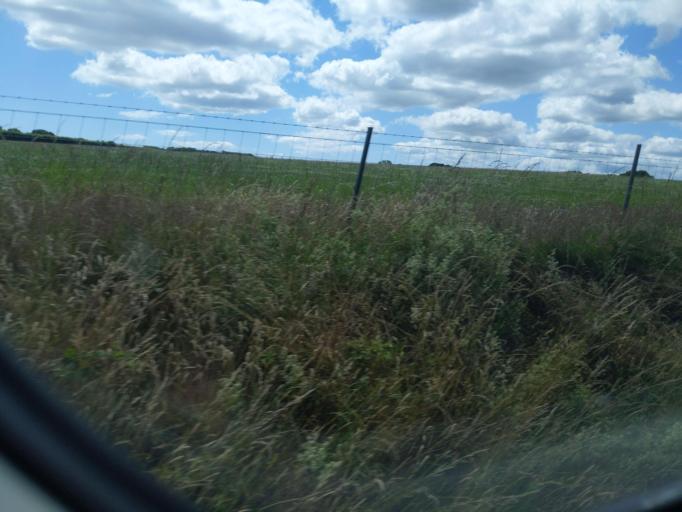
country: GB
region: England
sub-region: Cornwall
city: Liskeard
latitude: 50.4312
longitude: -4.4213
